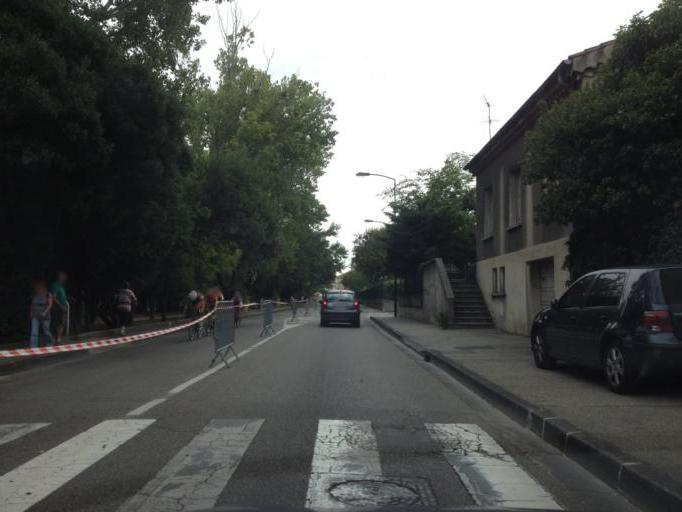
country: FR
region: Rhone-Alpes
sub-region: Departement de la Drome
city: Montelimar
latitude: 44.5607
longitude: 4.7461
